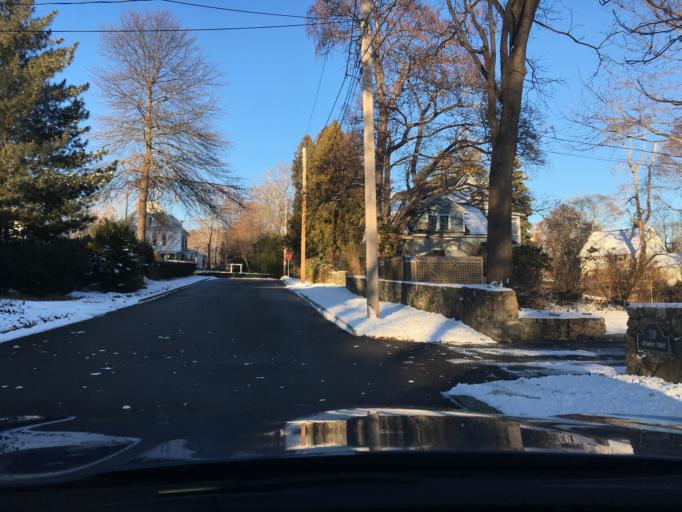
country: US
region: Rhode Island
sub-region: Kent County
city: East Greenwich
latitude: 41.6598
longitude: -71.4565
